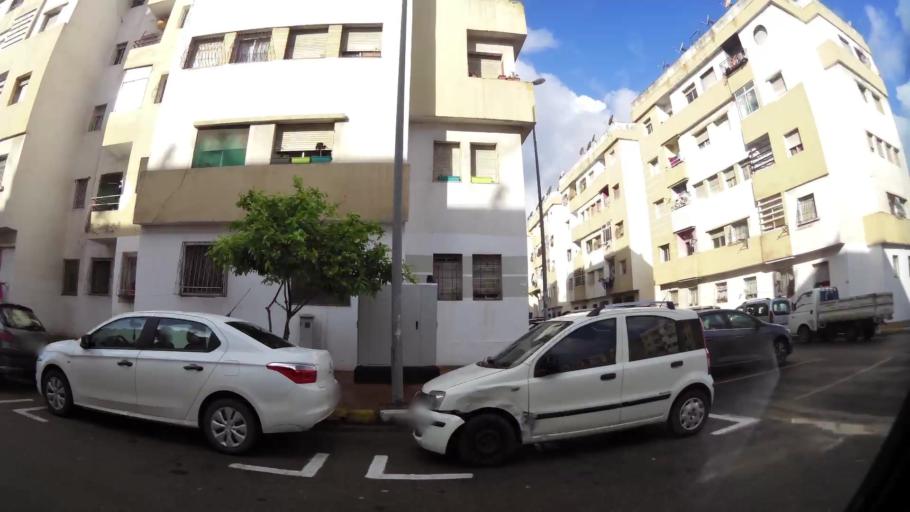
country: MA
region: Grand Casablanca
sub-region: Mediouna
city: Tit Mellil
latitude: 33.6007
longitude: -7.5332
